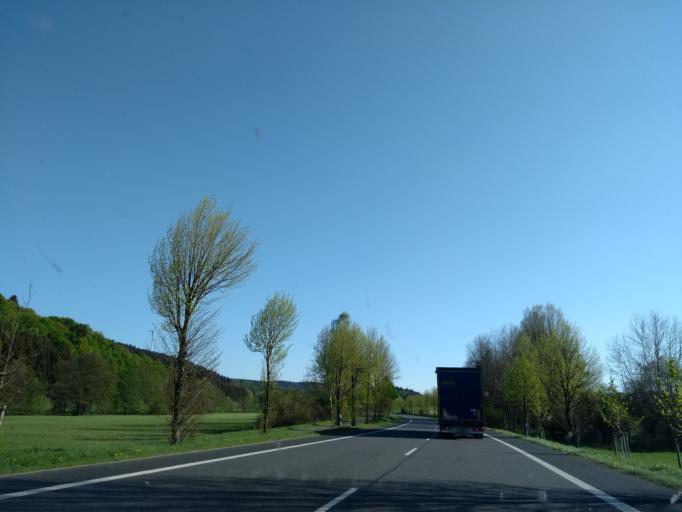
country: DE
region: Hesse
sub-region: Regierungsbezirk Giessen
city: Breidenbach
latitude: 50.8385
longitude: 8.3872
